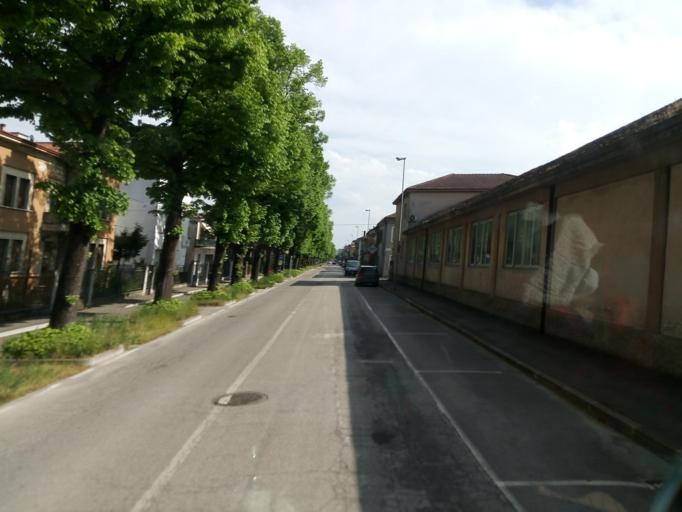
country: IT
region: Veneto
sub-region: Provincia di Verona
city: Angiari
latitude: 45.1991
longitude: 11.3128
